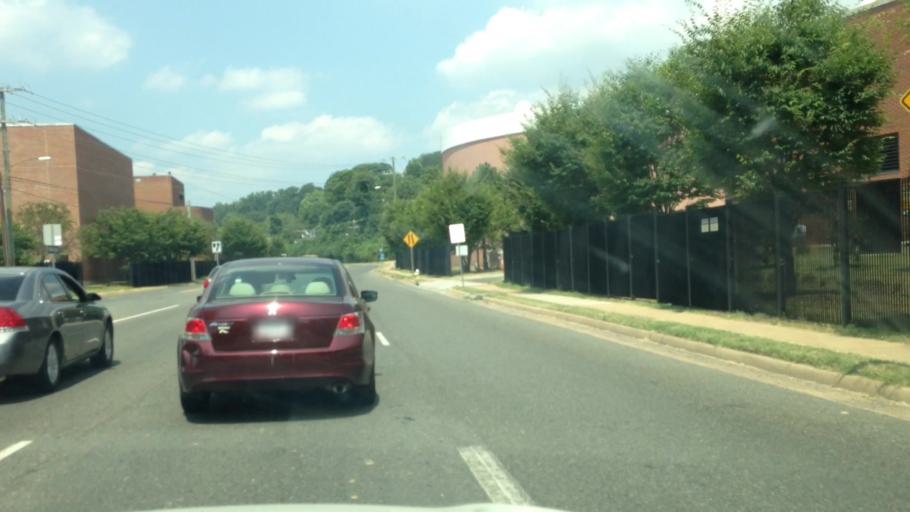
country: US
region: Virginia
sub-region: City of Alexandria
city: Alexandria
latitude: 38.8431
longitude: -77.0553
